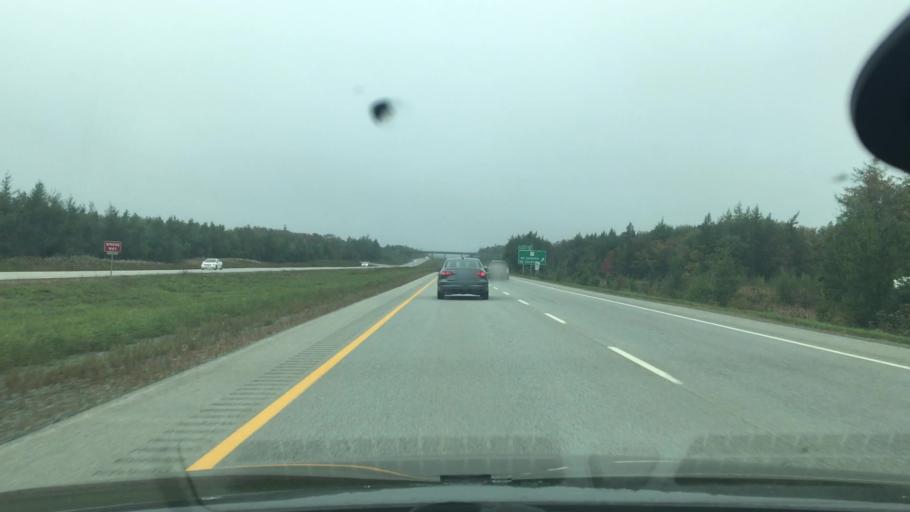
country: CA
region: Nova Scotia
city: Dartmouth
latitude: 44.8362
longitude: -63.7975
